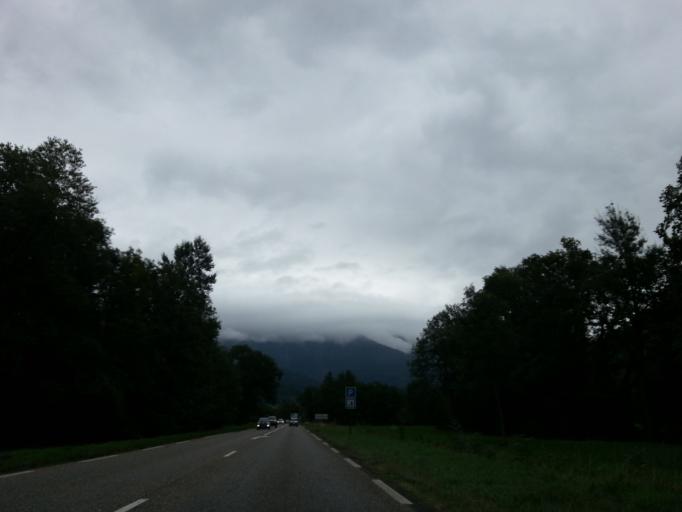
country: FR
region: Rhone-Alpes
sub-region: Departement de la Haute-Savoie
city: Faverges
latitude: 45.7585
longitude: 6.2654
